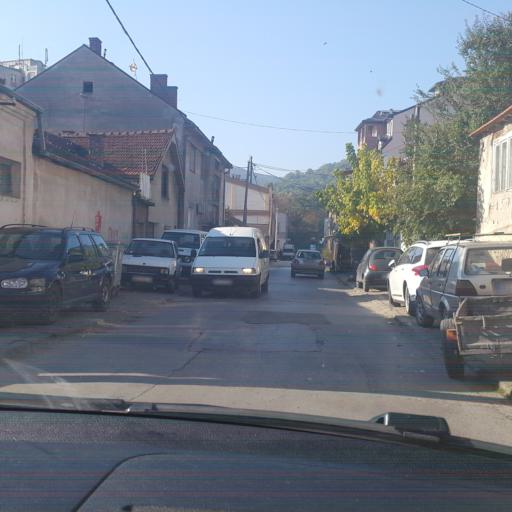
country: RS
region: Central Serbia
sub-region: Toplicki Okrug
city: Prokuplje
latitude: 43.2331
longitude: 21.5840
